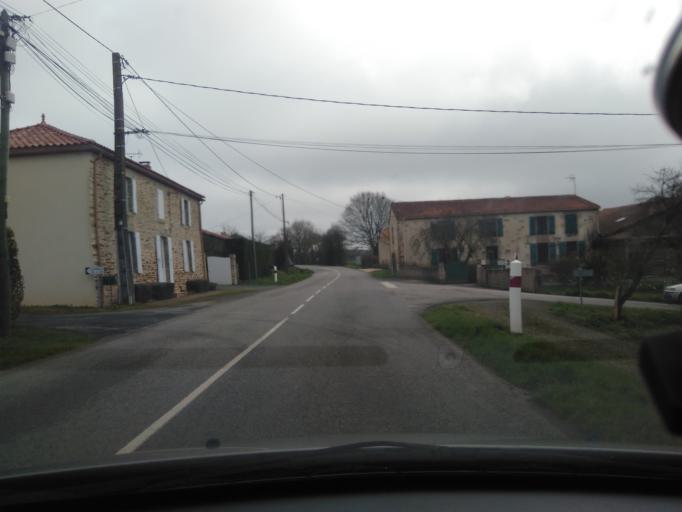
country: FR
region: Pays de la Loire
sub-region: Departement de la Vendee
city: La Ferriere
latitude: 46.7202
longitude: -1.2838
